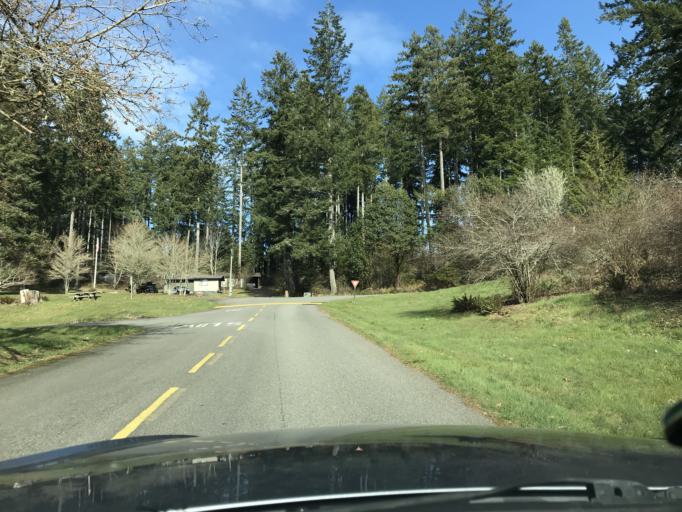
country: US
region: Washington
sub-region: Pierce County
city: Longbranch
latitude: 47.2257
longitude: -122.8082
